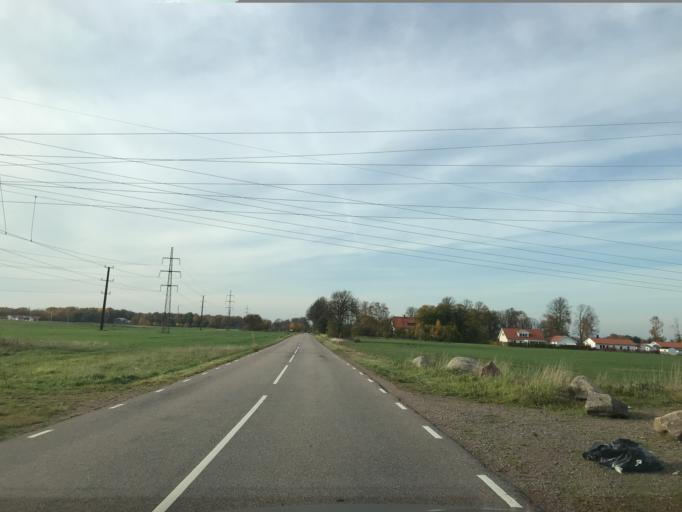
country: SE
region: Skane
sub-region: Helsingborg
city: Hyllinge
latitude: 56.0996
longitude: 12.8800
